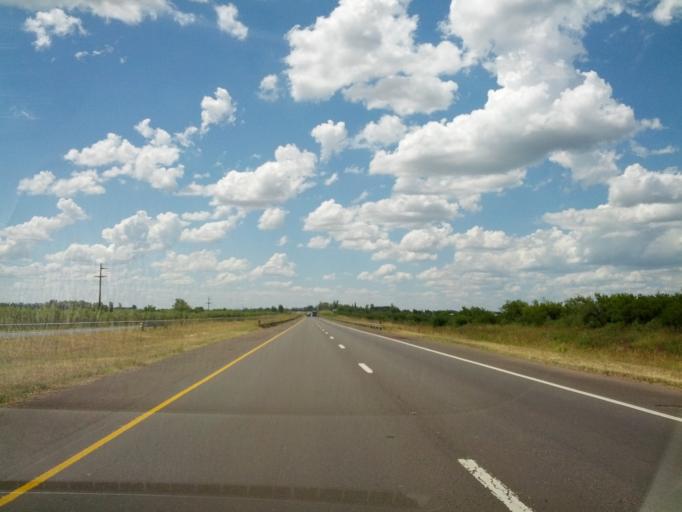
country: AR
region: Entre Rios
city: Concepcion del Uruguay
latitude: -32.4214
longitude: -58.2821
